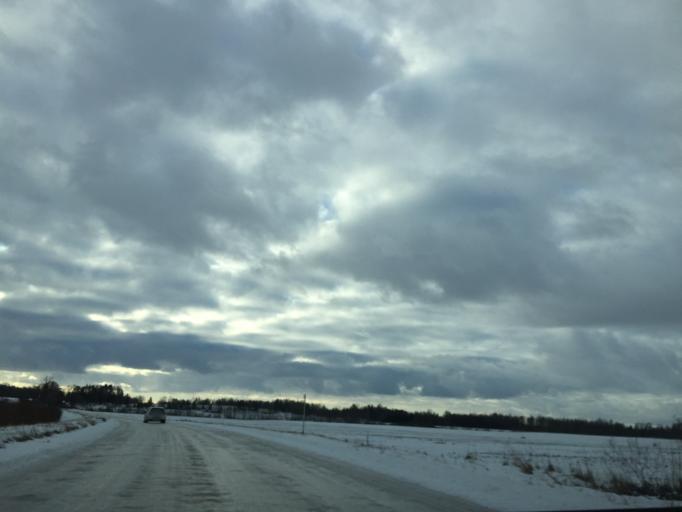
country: LV
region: Lielvarde
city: Lielvarde
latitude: 56.5879
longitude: 24.7344
